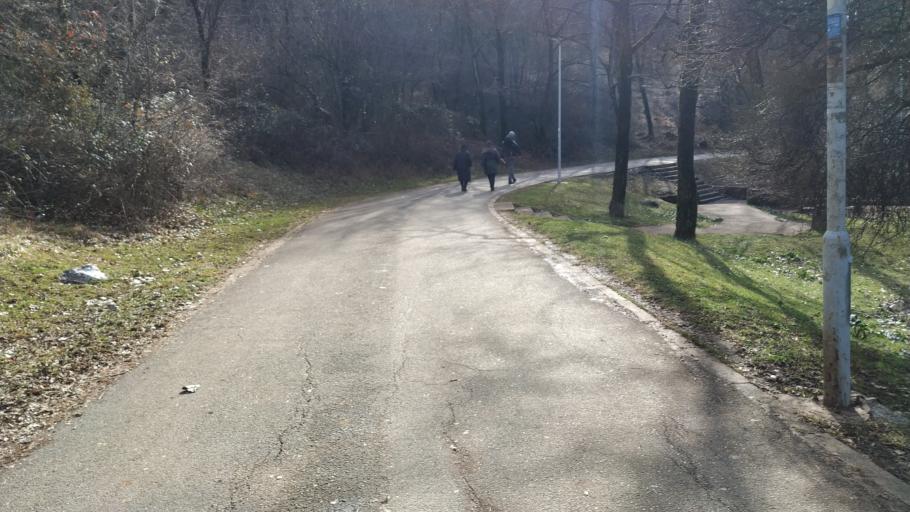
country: ME
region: Opstina Niksic
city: Niksic
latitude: 42.7671
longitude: 18.9563
